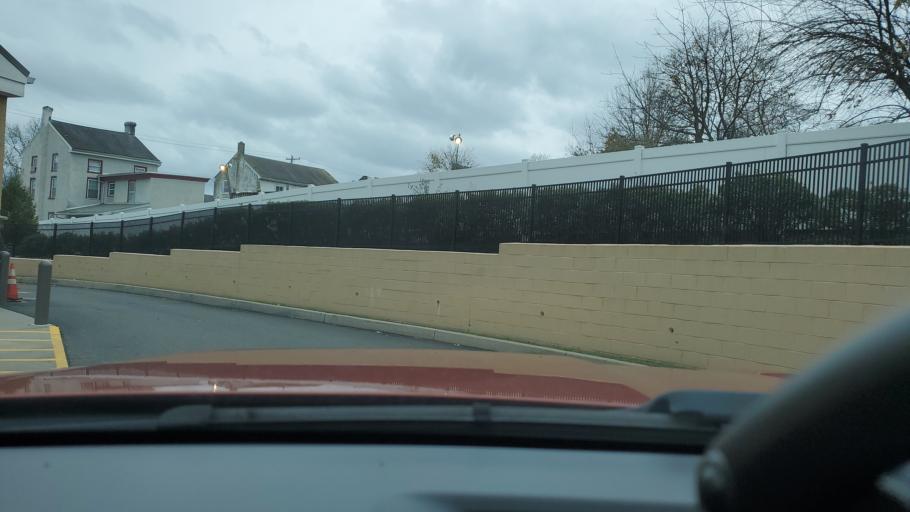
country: US
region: Pennsylvania
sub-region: Montgomery County
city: Spring Mount
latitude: 40.2779
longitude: -75.4811
